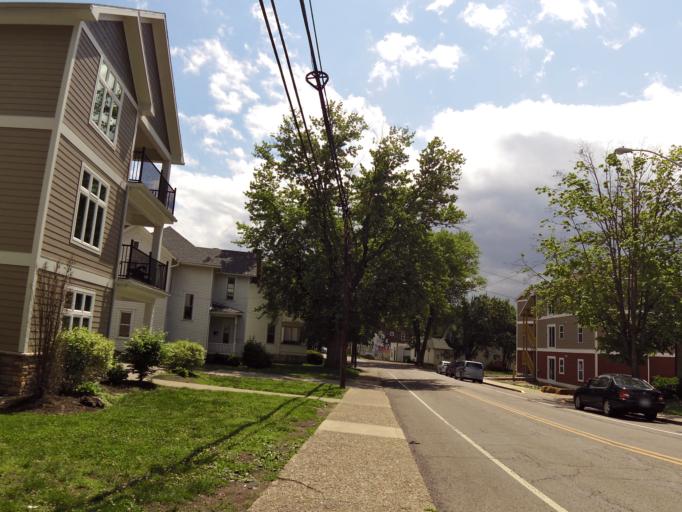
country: US
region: Ohio
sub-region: Athens County
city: Athens
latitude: 39.3300
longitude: -82.0980
